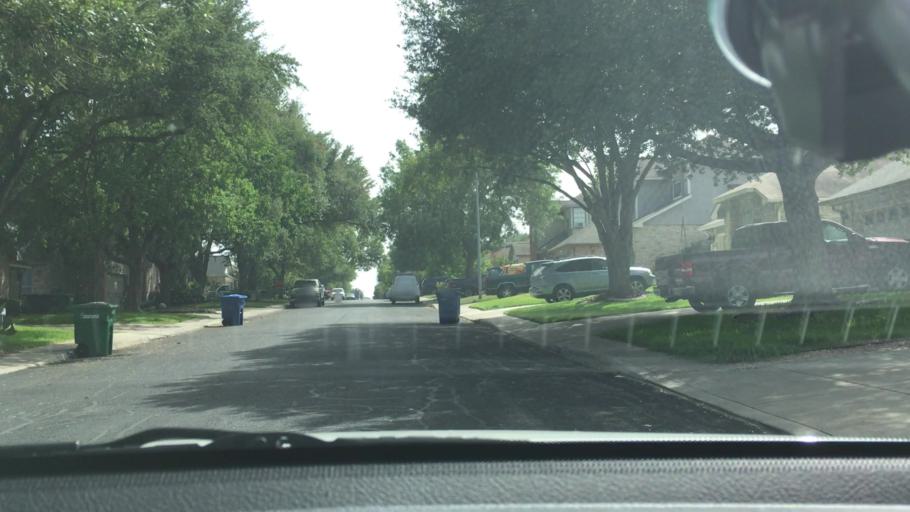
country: US
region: Texas
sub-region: Bexar County
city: Live Oak
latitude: 29.5783
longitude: -98.3804
